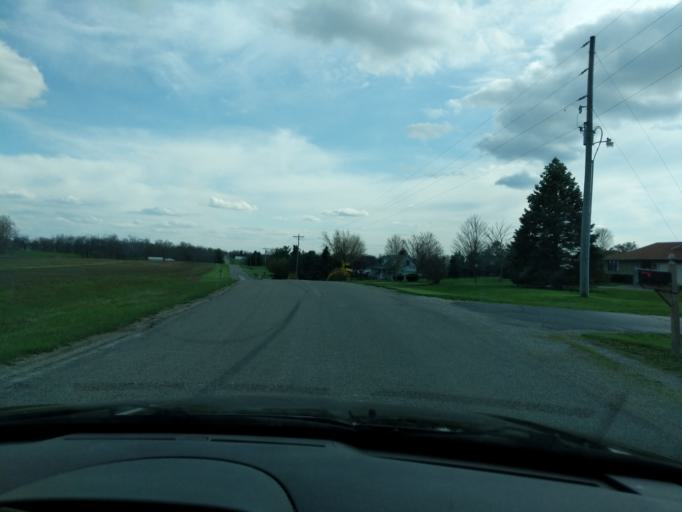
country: US
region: Ohio
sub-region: Champaign County
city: Urbana
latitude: 40.1501
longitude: -83.6483
